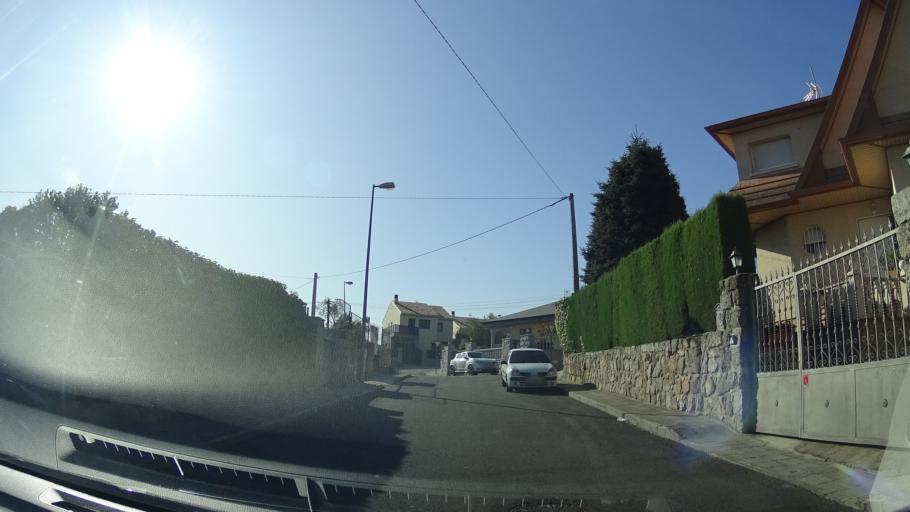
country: ES
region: Madrid
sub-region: Provincia de Madrid
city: Colmenarejo
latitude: 40.5593
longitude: -4.0193
